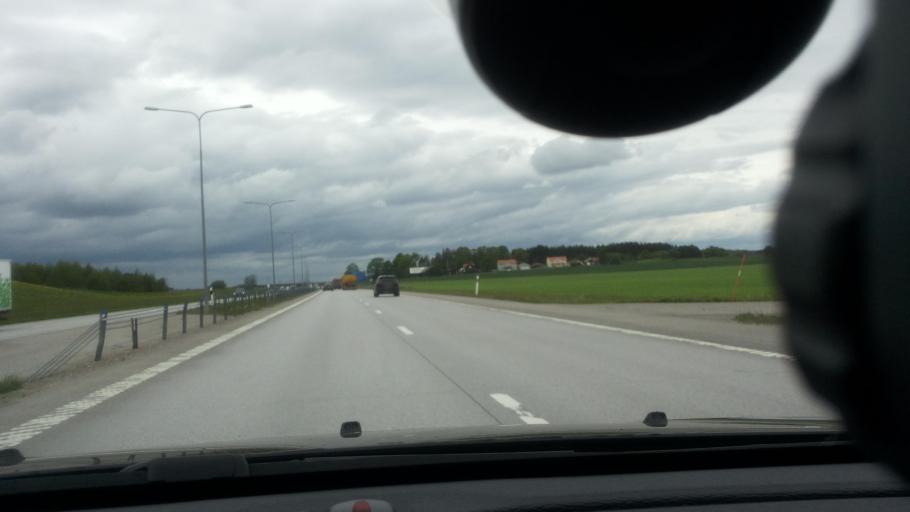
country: SE
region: Uppsala
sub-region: Uppsala Kommun
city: Saevja
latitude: 59.8738
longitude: 17.6996
